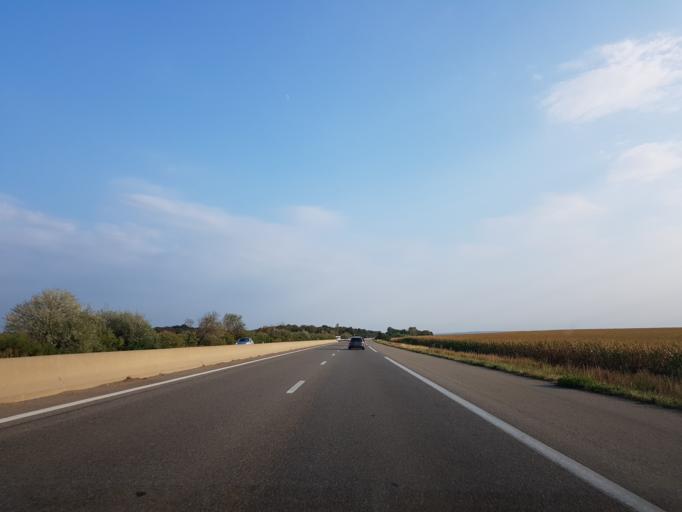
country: FR
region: Alsace
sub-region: Departement du Haut-Rhin
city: Battenheim
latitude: 47.8549
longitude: 7.3941
